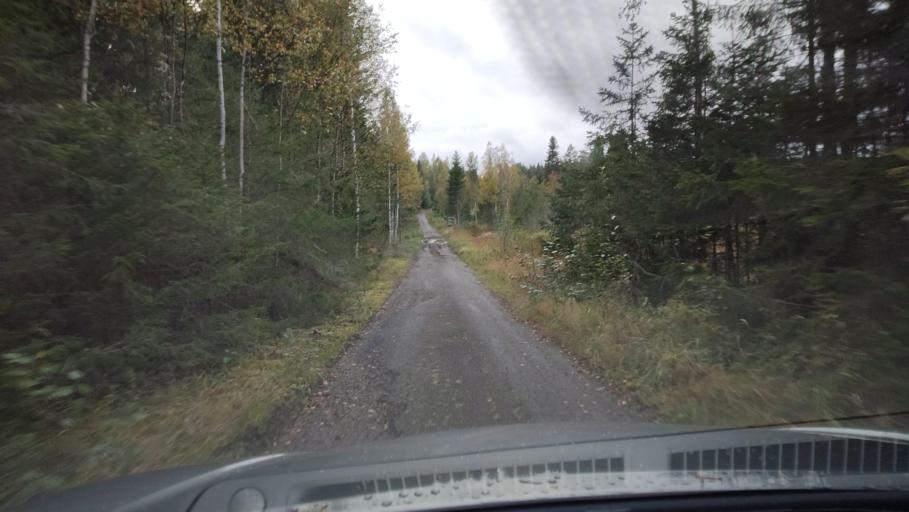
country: FI
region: Ostrobothnia
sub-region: Sydosterbotten
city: Kristinestad
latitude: 62.2695
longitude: 21.4537
